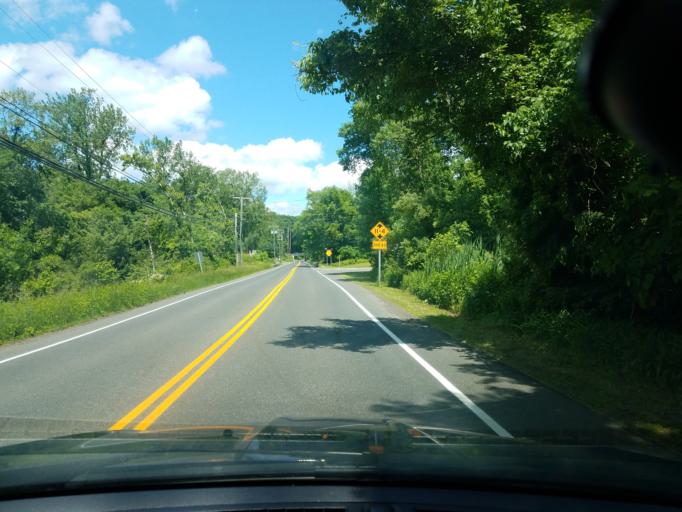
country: US
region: Connecticut
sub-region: Fairfield County
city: Bethel
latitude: 41.3550
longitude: -73.4158
